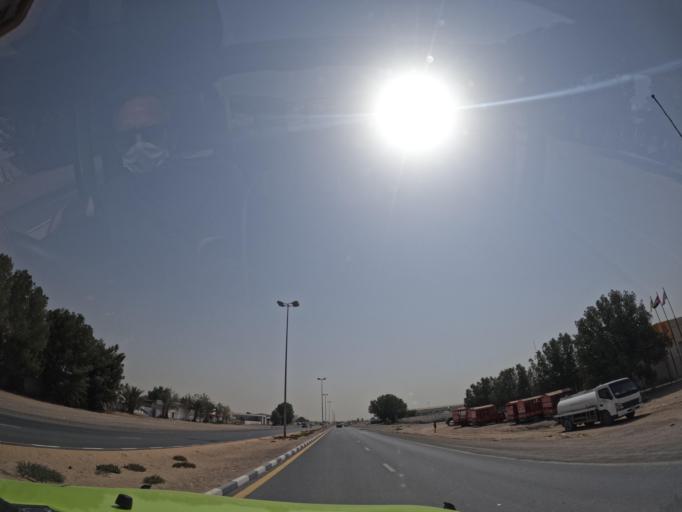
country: AE
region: Umm al Qaywayn
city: Umm al Qaywayn
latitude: 25.5016
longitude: 55.5619
